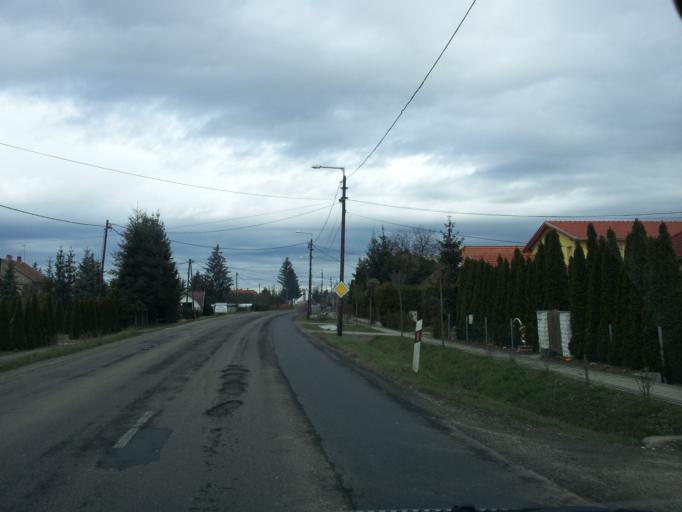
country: HU
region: Vas
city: Gencsapati
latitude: 47.3372
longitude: 16.5813
